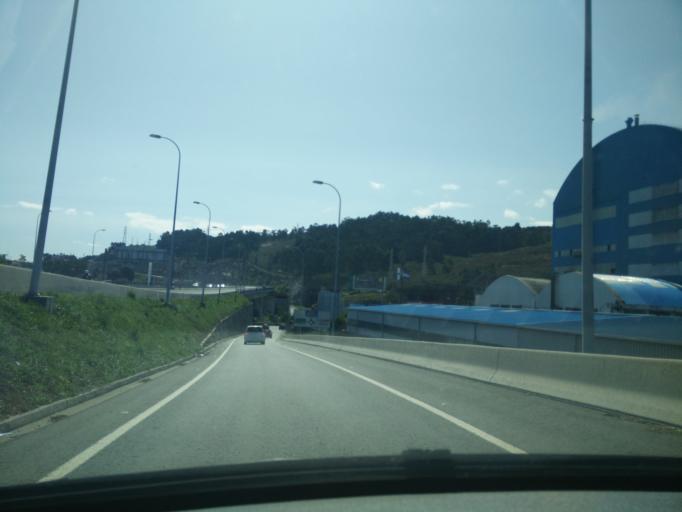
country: ES
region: Galicia
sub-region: Provincia da Coruna
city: A Coruna
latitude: 43.3465
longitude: -8.4336
